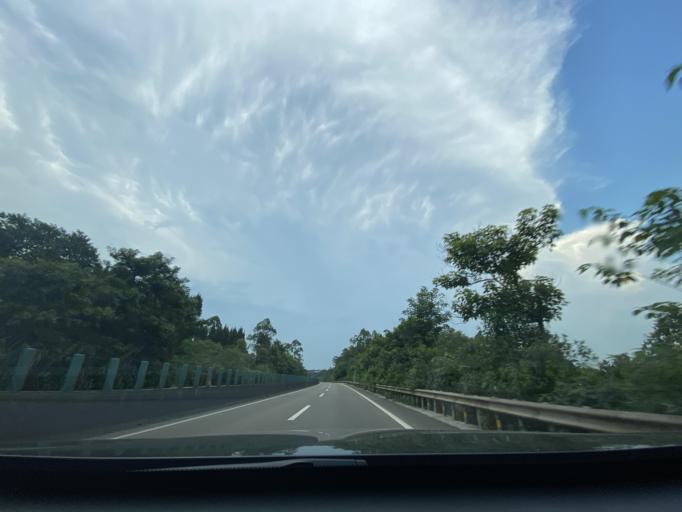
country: CN
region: Sichuan
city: Neijiang
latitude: 29.6483
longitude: 104.9852
